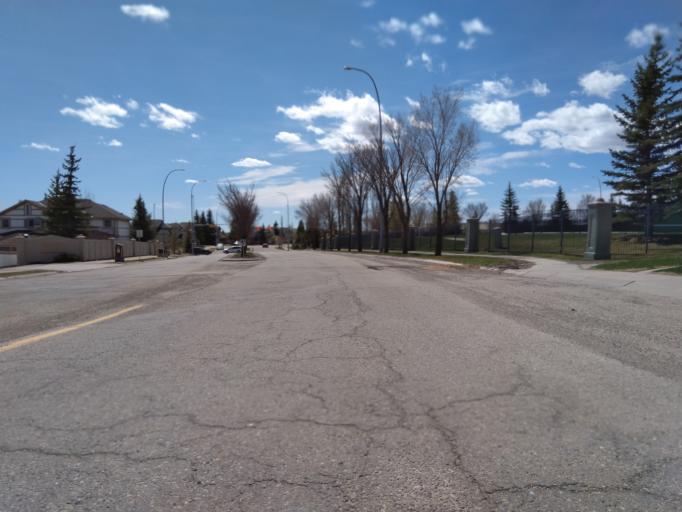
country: CA
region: Alberta
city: Calgary
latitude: 51.1260
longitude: -114.2436
